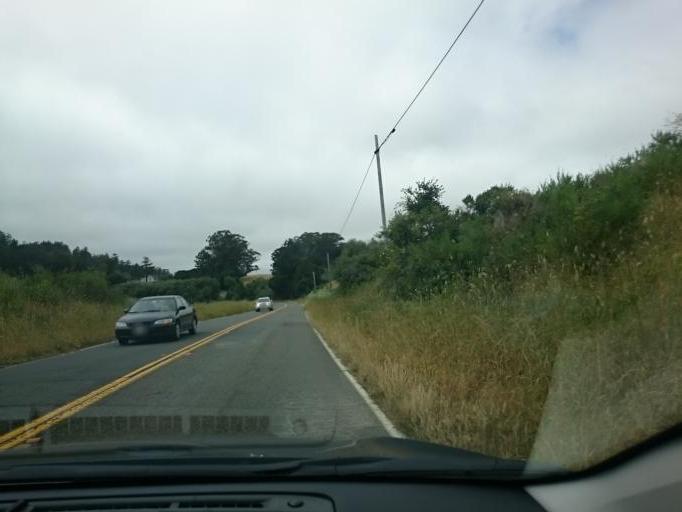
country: US
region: California
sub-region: Marin County
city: Lagunitas-Forest Knolls
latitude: 38.0059
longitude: -122.7605
